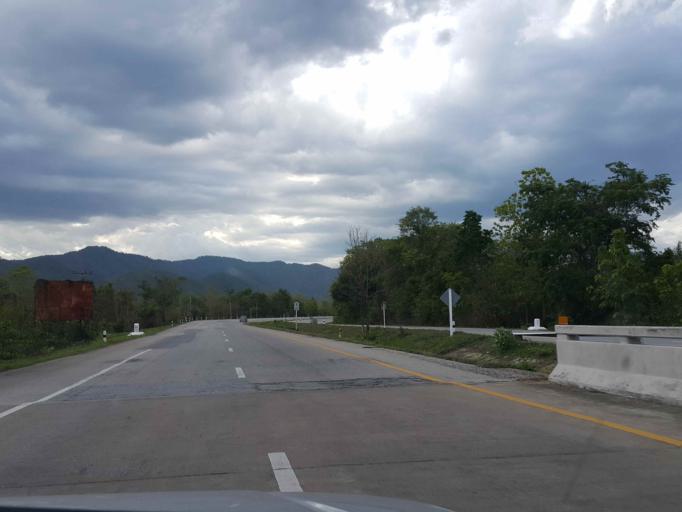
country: TH
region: Lampang
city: Thoen
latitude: 17.7411
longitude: 99.2321
